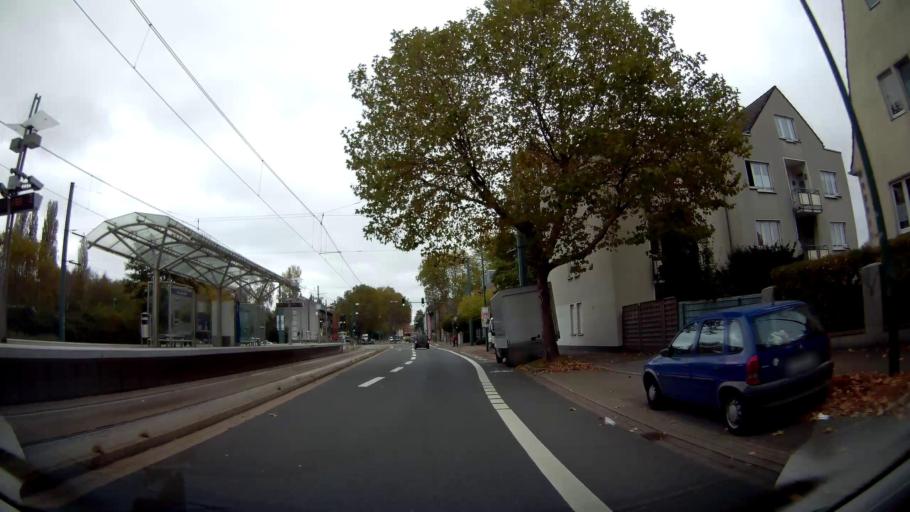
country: DE
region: North Rhine-Westphalia
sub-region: Regierungsbezirk Munster
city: Gladbeck
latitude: 51.5280
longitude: 7.0100
